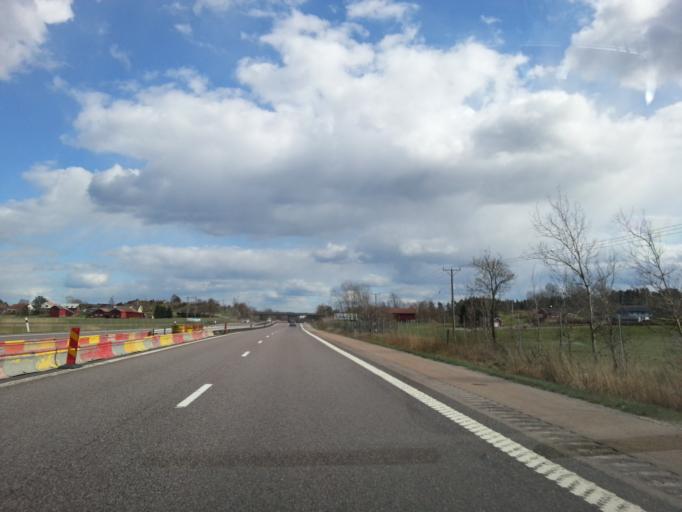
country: SE
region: Vaestra Goetaland
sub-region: Kungalvs Kommun
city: Kungalv
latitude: 57.9016
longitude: 11.9170
